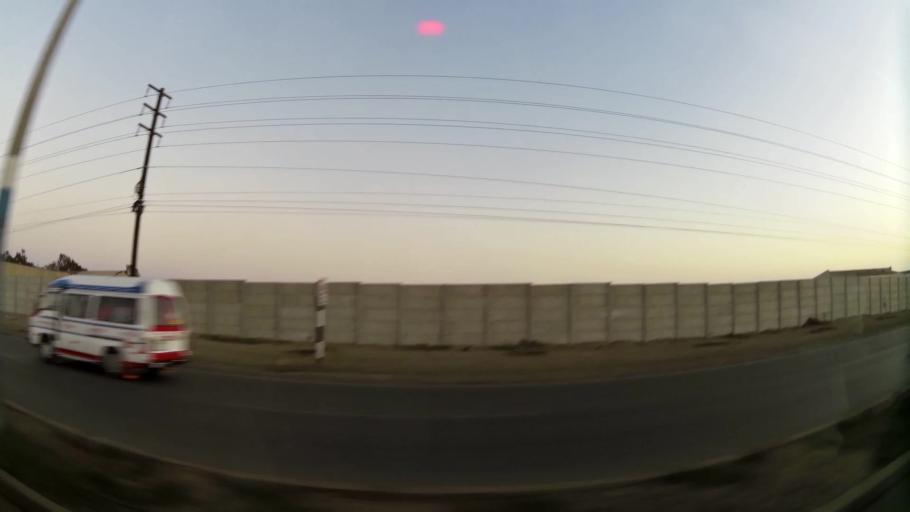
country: PE
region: Ica
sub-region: Provincia de Pisco
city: Pisco
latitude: -13.7114
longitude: -76.1861
